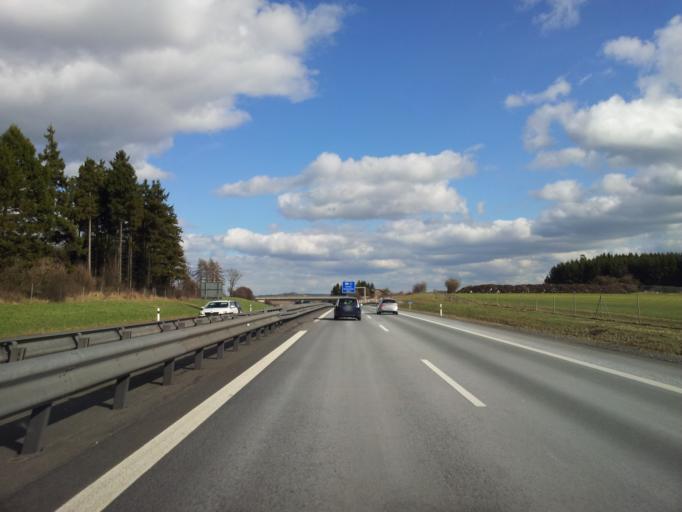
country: DE
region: Bavaria
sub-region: Upper Franconia
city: Feilitzsch
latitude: 50.3760
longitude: 11.9254
